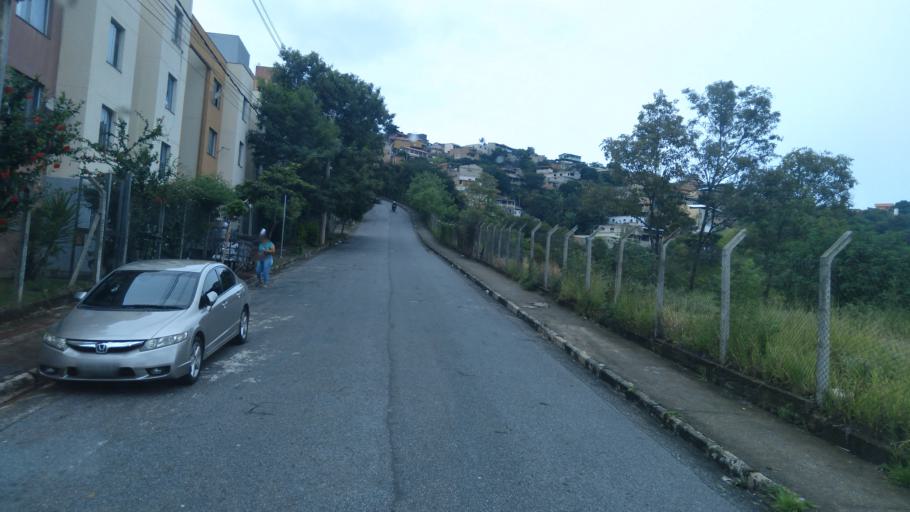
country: BR
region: Minas Gerais
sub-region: Belo Horizonte
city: Belo Horizonte
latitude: -19.9118
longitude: -43.8836
